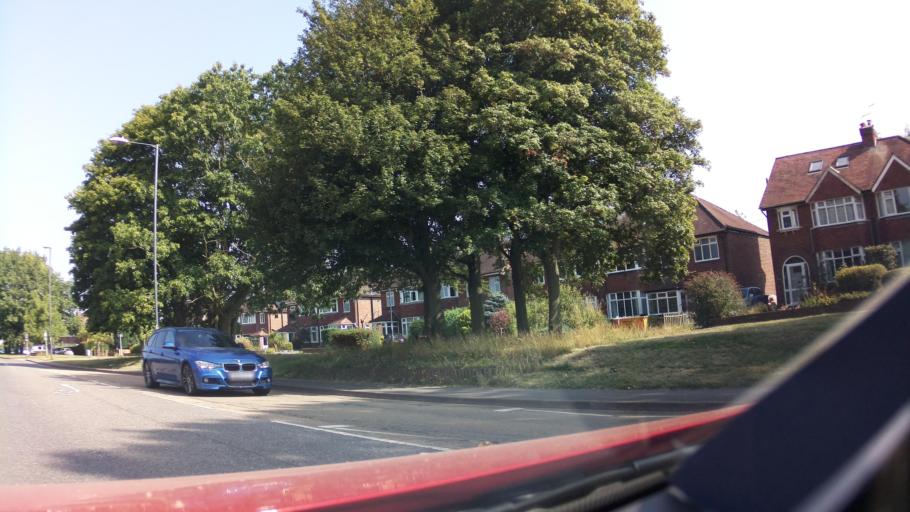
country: GB
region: England
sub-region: Derby
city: Derby
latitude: 52.9424
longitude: -1.5035
